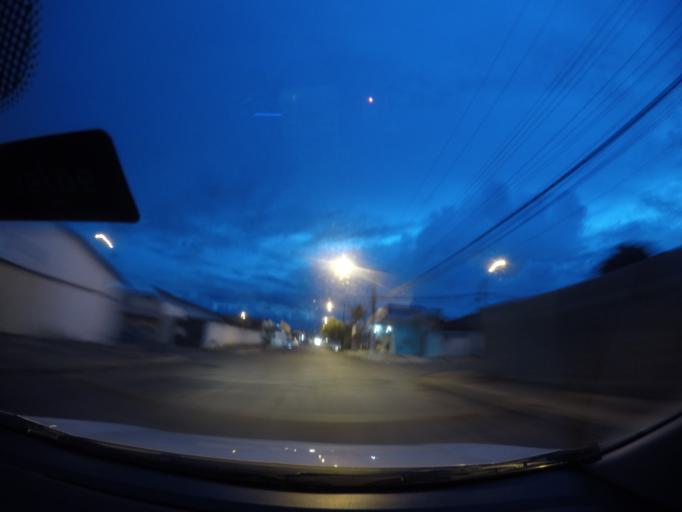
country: BR
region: Goias
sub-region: Goiania
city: Goiania
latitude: -16.7257
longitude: -49.3676
